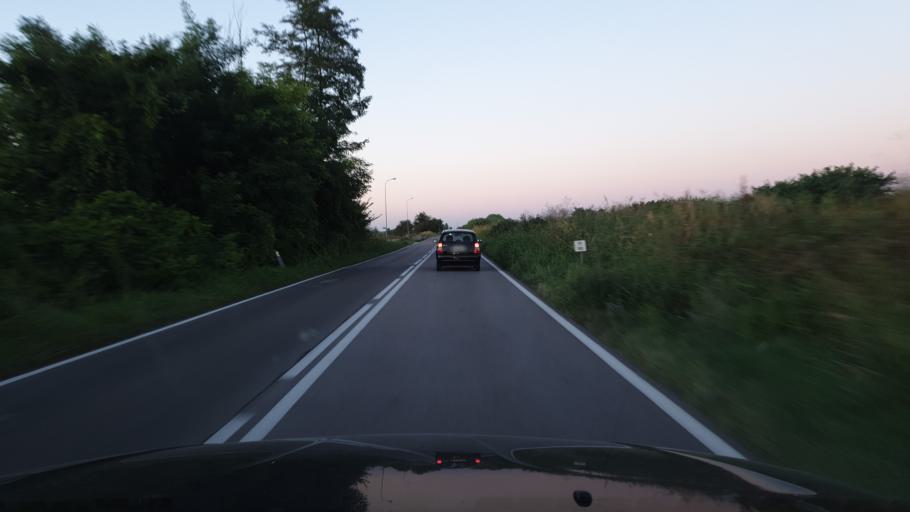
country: IT
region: Emilia-Romagna
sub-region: Provincia di Bologna
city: Minerbio
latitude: 44.6324
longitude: 11.4659
